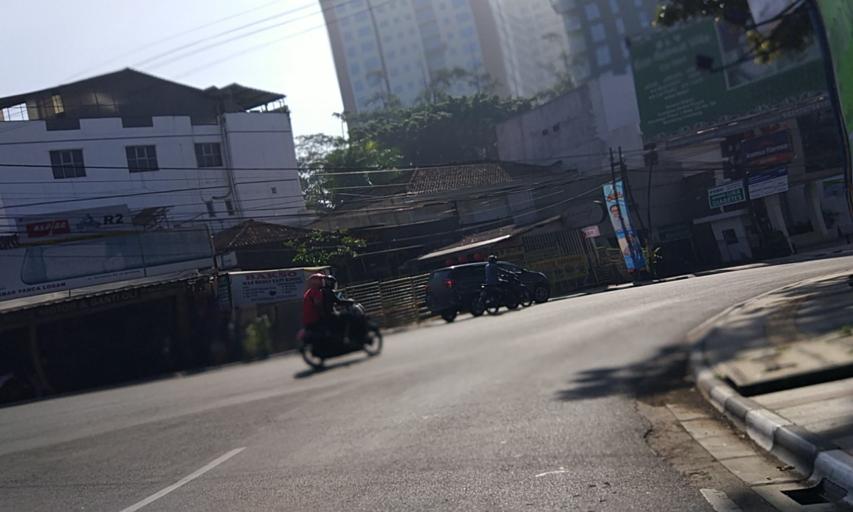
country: ID
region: West Java
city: Bandung
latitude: -6.8830
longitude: 107.6014
